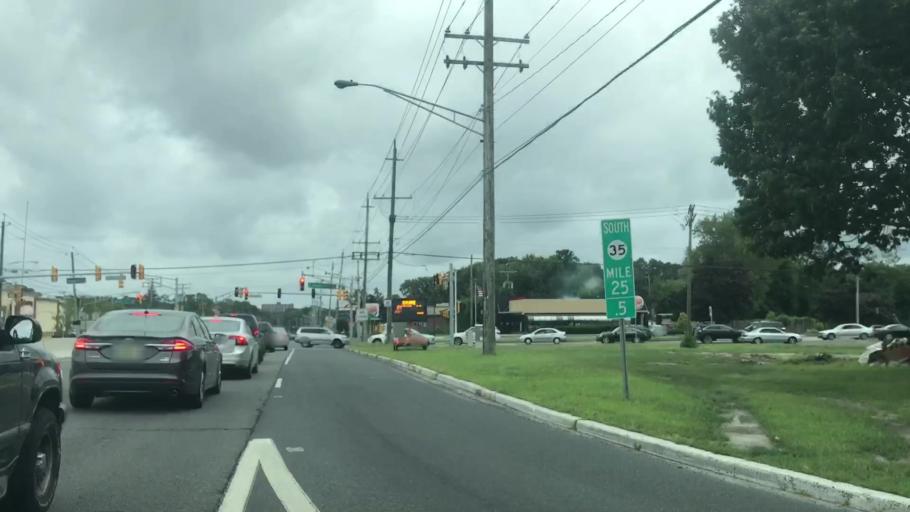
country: US
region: New Jersey
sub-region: Monmouth County
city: Wanamassa
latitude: 40.2364
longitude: -74.0379
